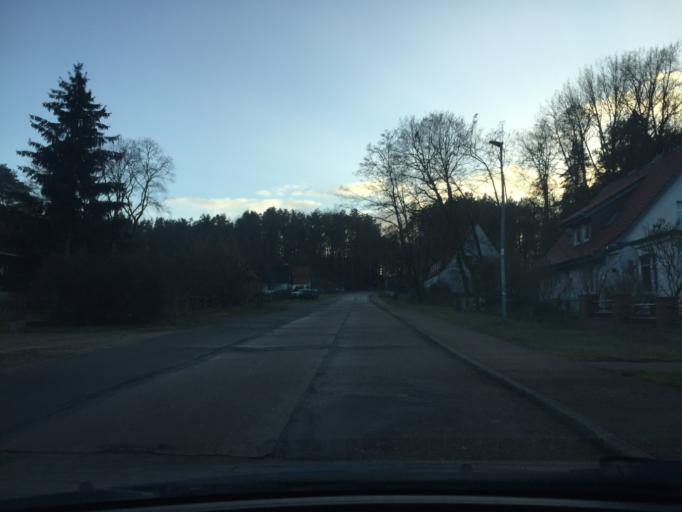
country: DE
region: Lower Saxony
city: Hitzacker
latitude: 53.1780
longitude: 10.9831
